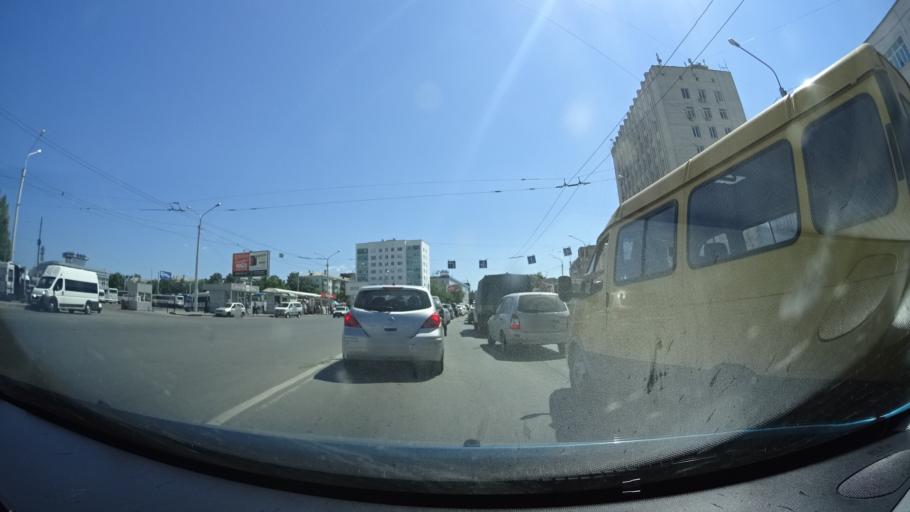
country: RU
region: Bashkortostan
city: Ufa
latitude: 54.7503
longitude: 55.9836
